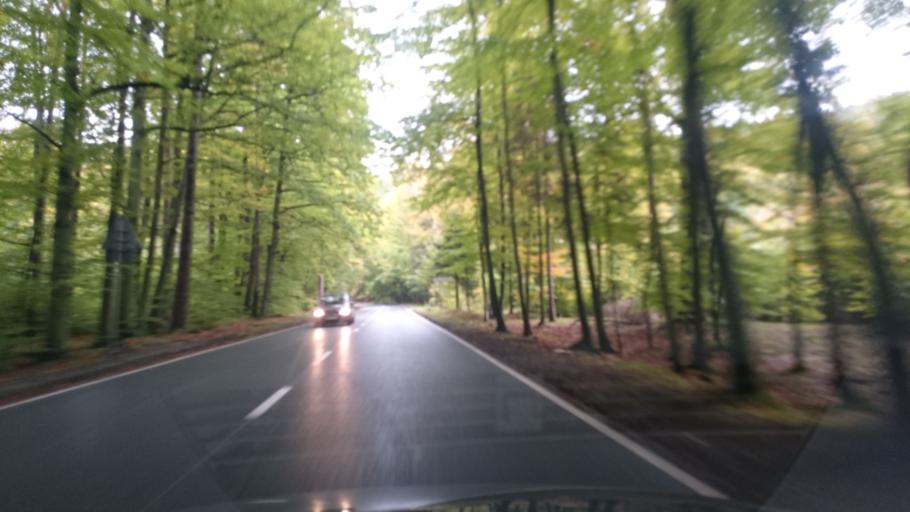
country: PL
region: Pomeranian Voivodeship
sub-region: Gdynia
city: Wielki Kack
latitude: 54.4560
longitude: 18.5177
